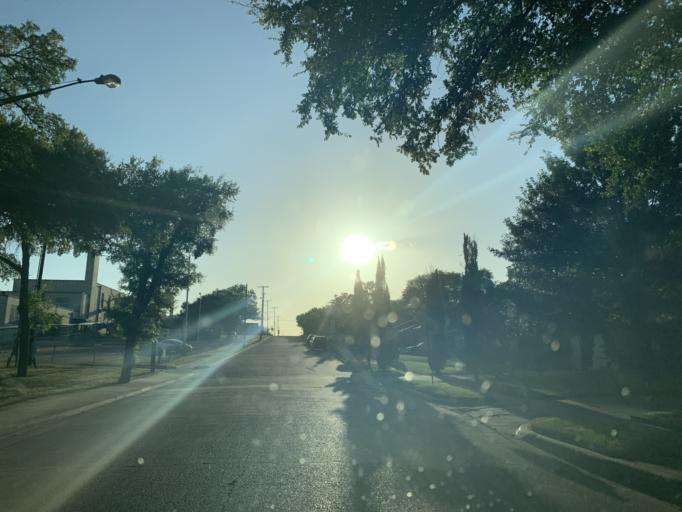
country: US
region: Texas
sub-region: Dallas County
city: Cockrell Hill
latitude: 32.6961
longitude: -96.8100
